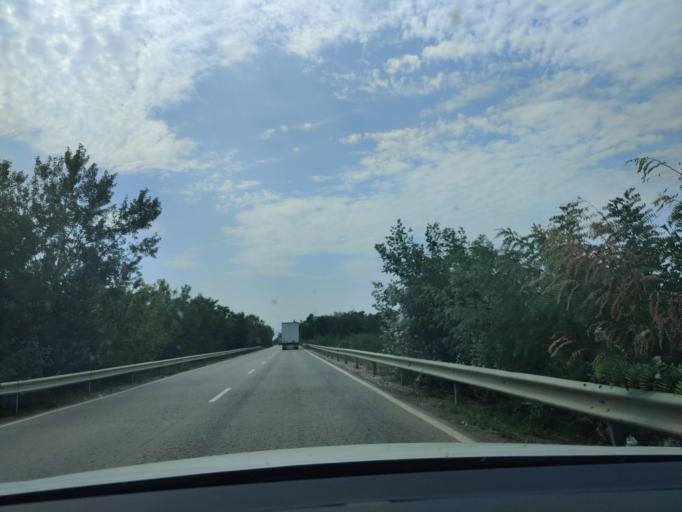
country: BG
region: Vidin
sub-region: Obshtina Dimovo
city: Dimovo
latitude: 43.8004
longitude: 22.7478
